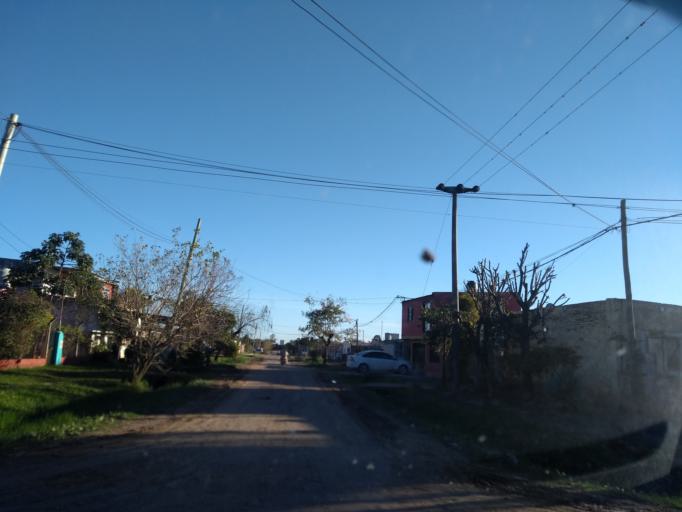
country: AR
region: Chaco
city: Barranqueras
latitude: -27.4907
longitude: -58.9361
